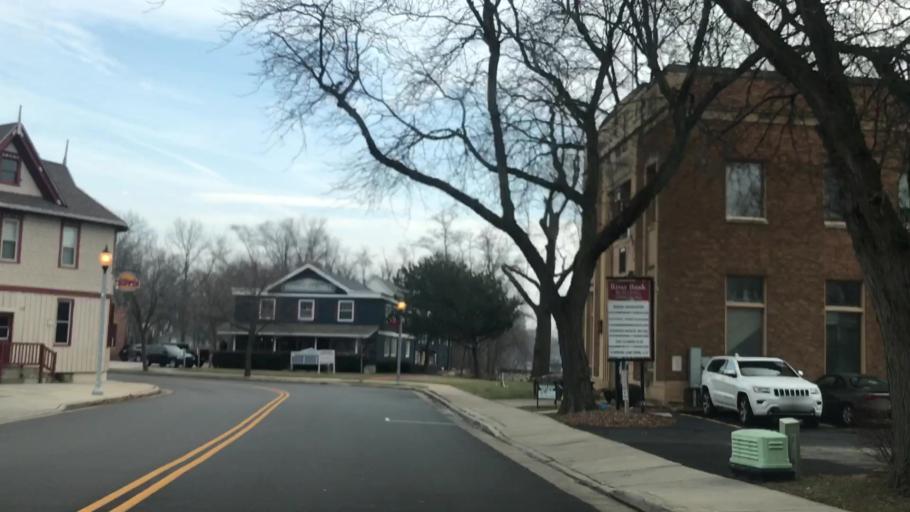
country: US
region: Wisconsin
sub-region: Ozaukee County
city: Mequon
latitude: 43.2305
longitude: -87.9832
